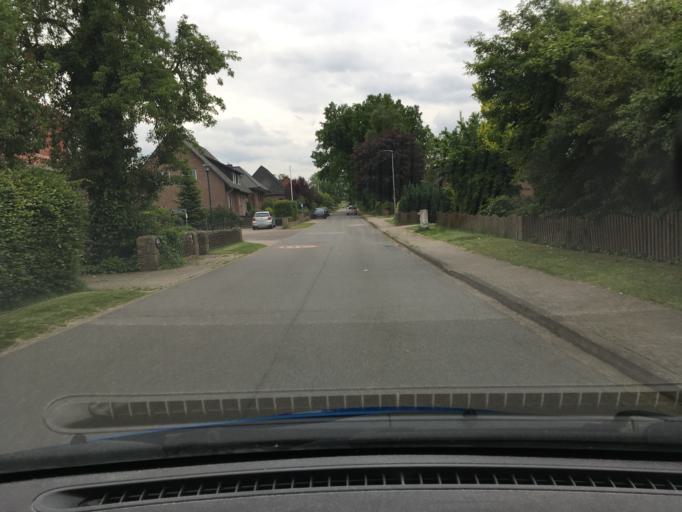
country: DE
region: Lower Saxony
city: Eyendorf
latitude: 53.2056
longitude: 10.1614
